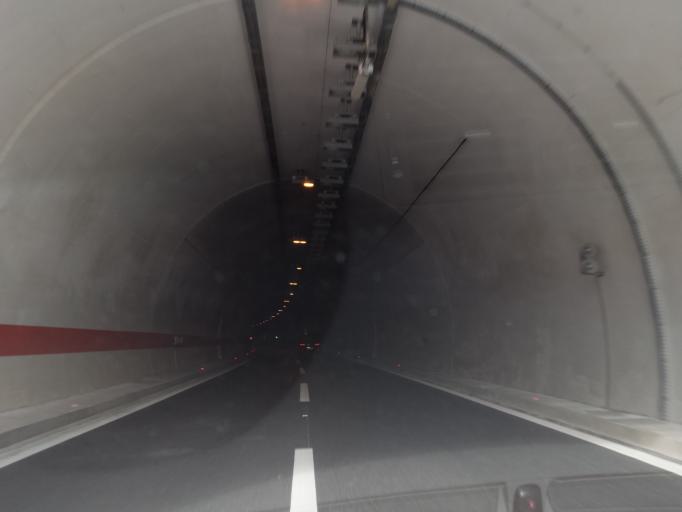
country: BA
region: Federation of Bosnia and Herzegovina
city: Vitina
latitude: 43.1616
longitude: 17.4722
